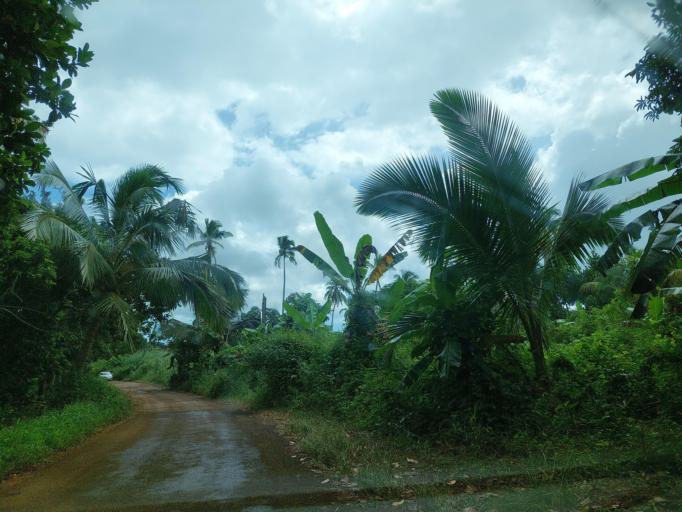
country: YT
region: M'Tsangamouji
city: M'Tsangamouji
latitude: -12.7510
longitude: 45.1187
